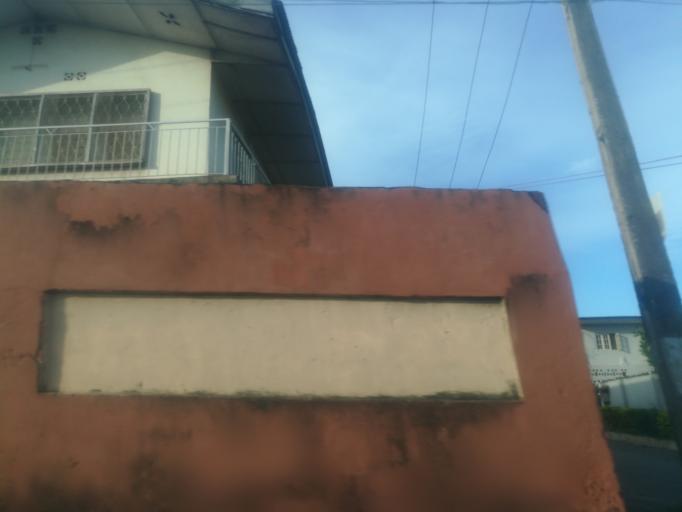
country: NG
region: Oyo
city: Ibadan
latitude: 7.3432
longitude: 3.8890
